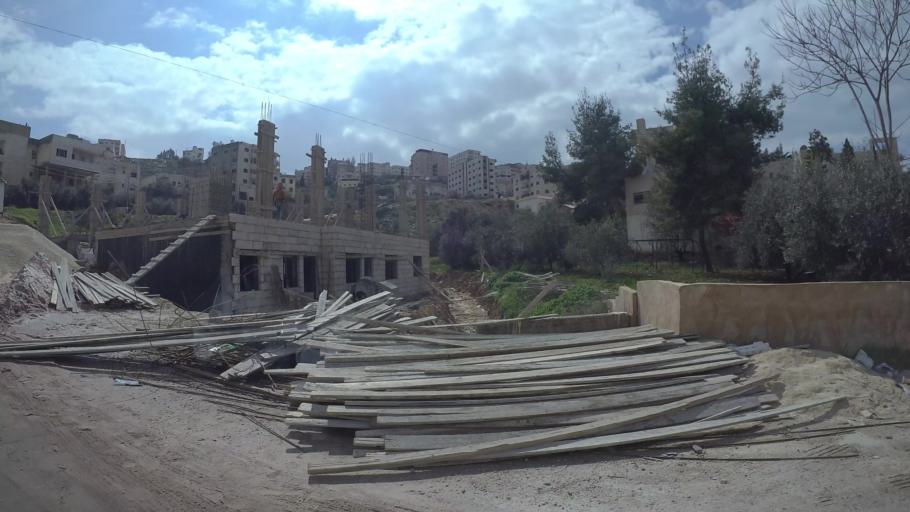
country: JO
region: Amman
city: Al Jubayhah
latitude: 32.0357
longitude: 35.8286
